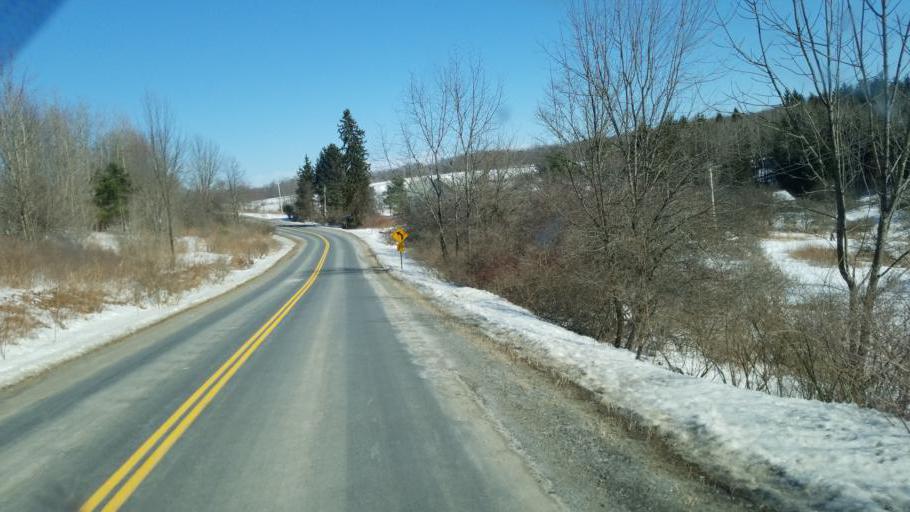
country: US
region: New York
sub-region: Allegany County
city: Andover
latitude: 42.0975
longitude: -77.7066
